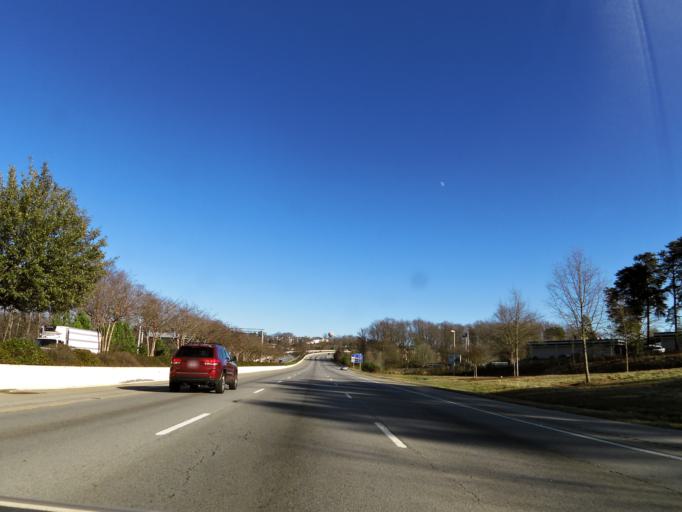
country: US
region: South Carolina
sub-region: Greenville County
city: Greenville
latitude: 34.8581
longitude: -82.3545
